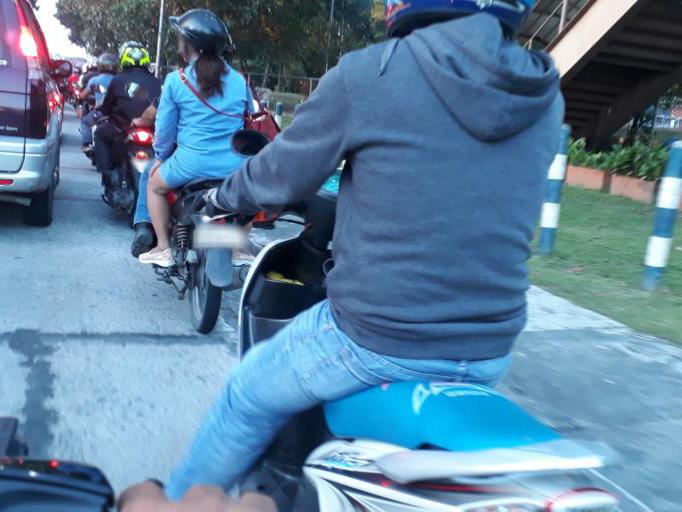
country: PH
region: Metro Manila
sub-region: Marikina
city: Calumpang
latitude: 14.6367
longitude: 121.0746
